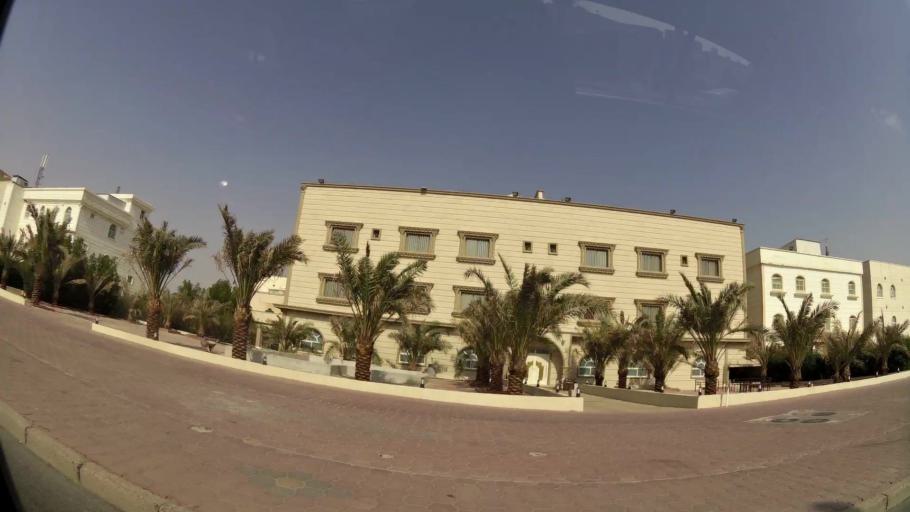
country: KW
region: Muhafazat al Jahra'
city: Al Jahra'
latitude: 29.3469
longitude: 47.6619
